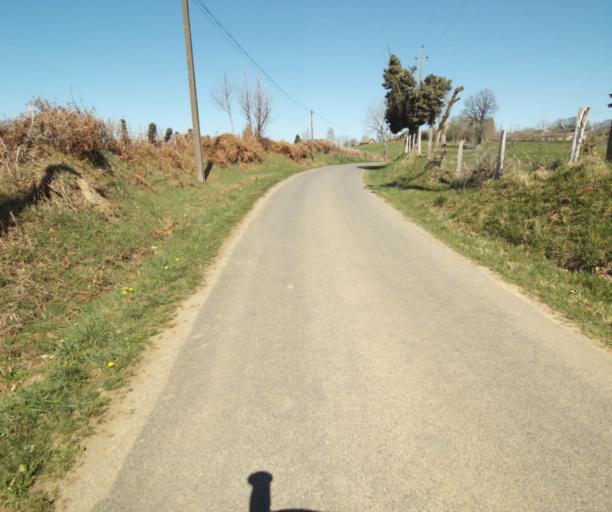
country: FR
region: Limousin
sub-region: Departement de la Correze
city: Saint-Clement
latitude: 45.3366
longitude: 1.7063
